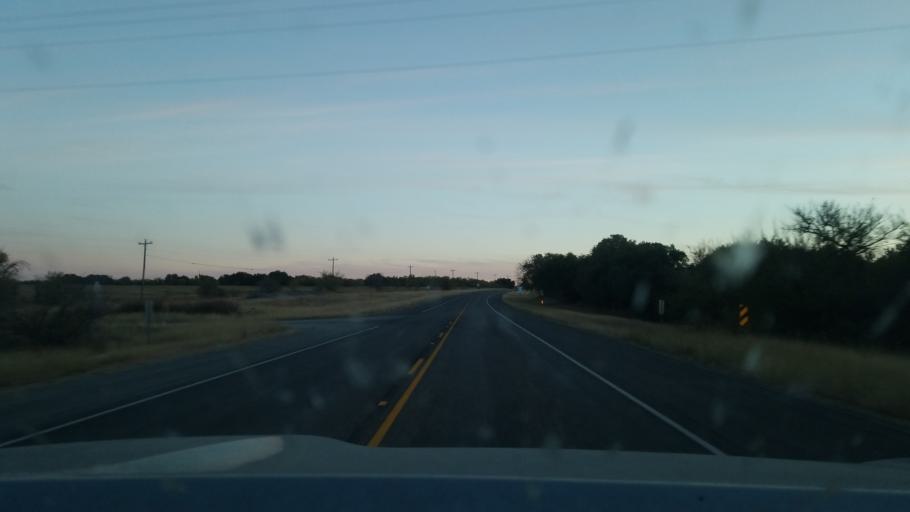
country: US
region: Texas
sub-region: Stephens County
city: Breckenridge
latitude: 32.5786
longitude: -98.8956
